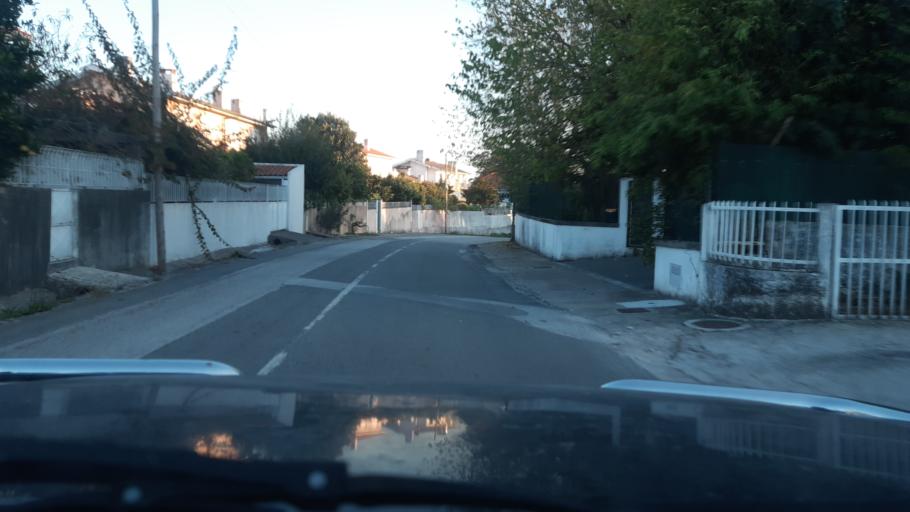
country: PT
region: Aveiro
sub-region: Agueda
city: Agueda
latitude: 40.5802
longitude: -8.4634
